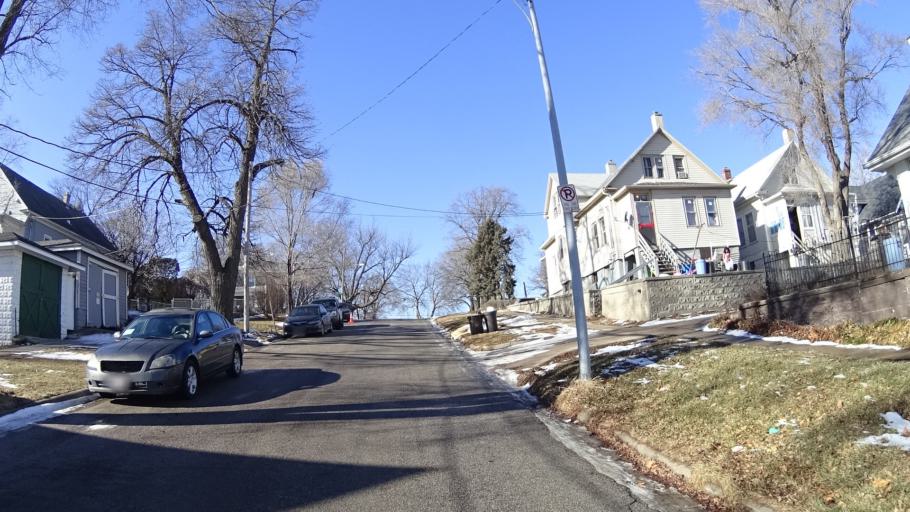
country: US
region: Nebraska
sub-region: Douglas County
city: Omaha
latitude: 41.2414
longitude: -95.9354
